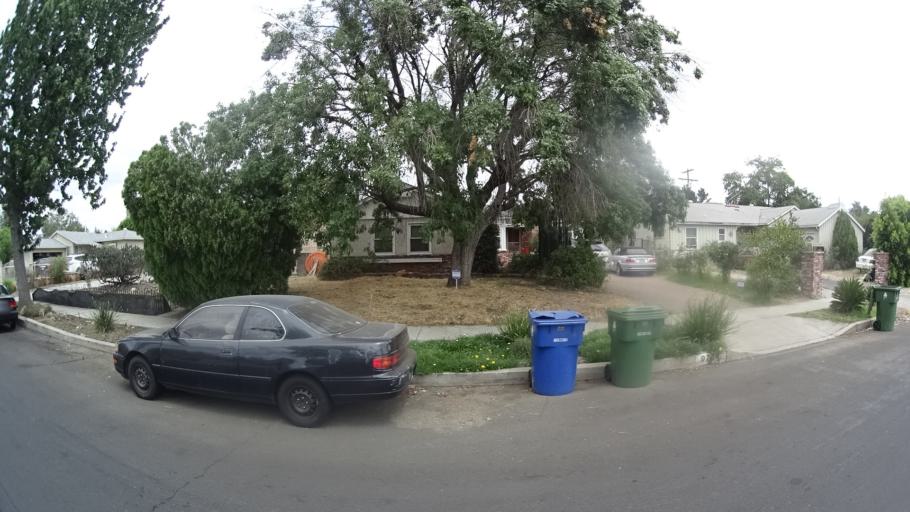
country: US
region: California
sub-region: Los Angeles County
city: San Fernando
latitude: 34.2478
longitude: -118.4530
